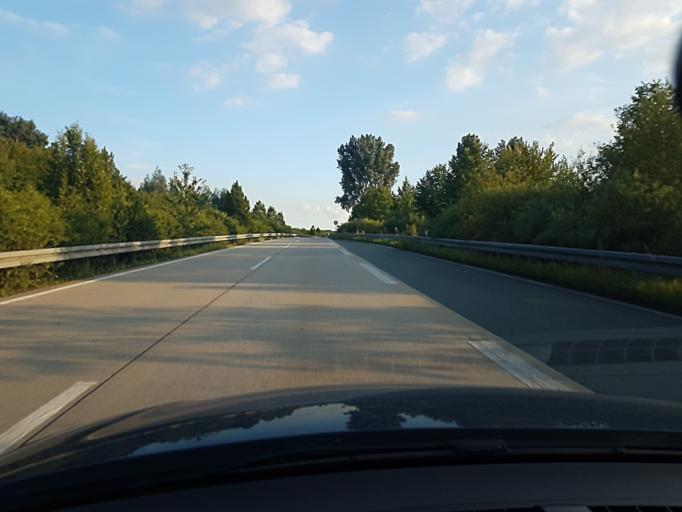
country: DE
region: North Rhine-Westphalia
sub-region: Regierungsbezirk Dusseldorf
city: Ratingen
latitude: 51.3054
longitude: 6.7743
